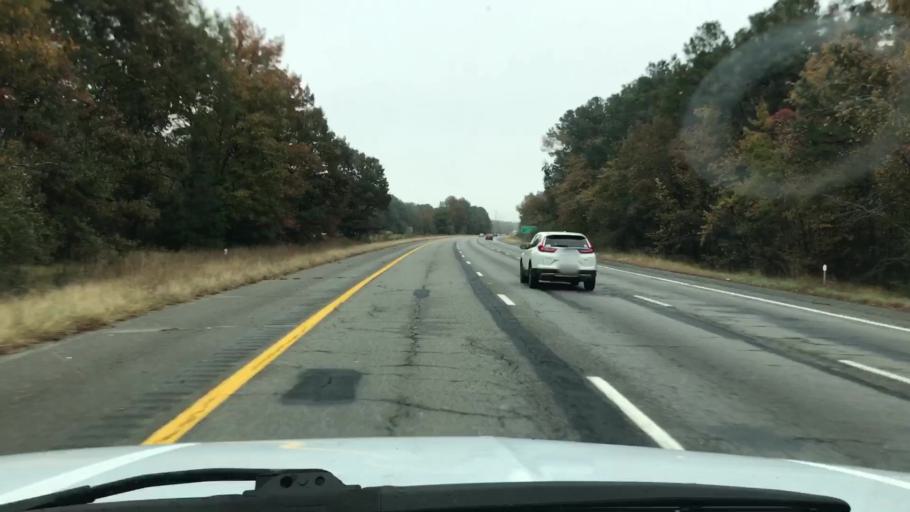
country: US
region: Virginia
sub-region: Henrico County
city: Glen Allen
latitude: 37.6812
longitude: -77.5201
